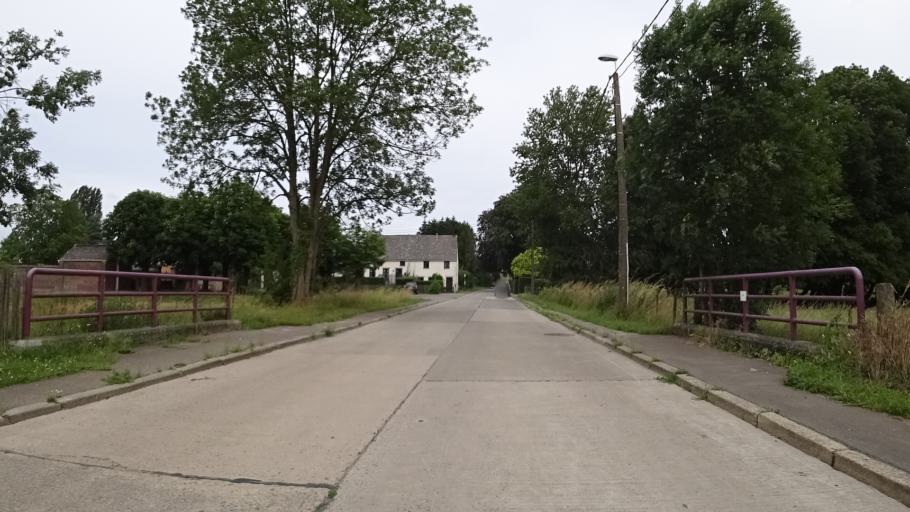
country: BE
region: Wallonia
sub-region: Province du Brabant Wallon
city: Walhain-Saint-Paul
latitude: 50.6424
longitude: 4.6735
